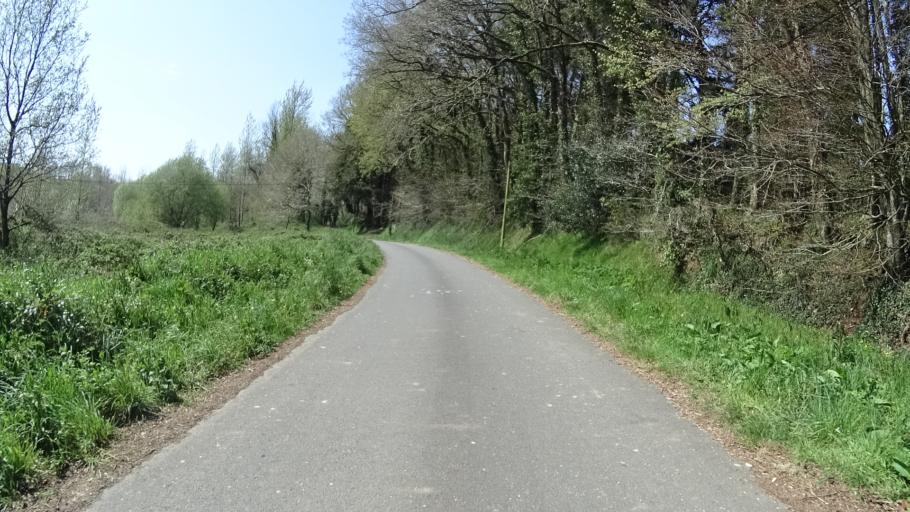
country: FR
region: Brittany
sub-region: Departement du Finistere
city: Sizun
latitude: 48.4129
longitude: -4.0868
